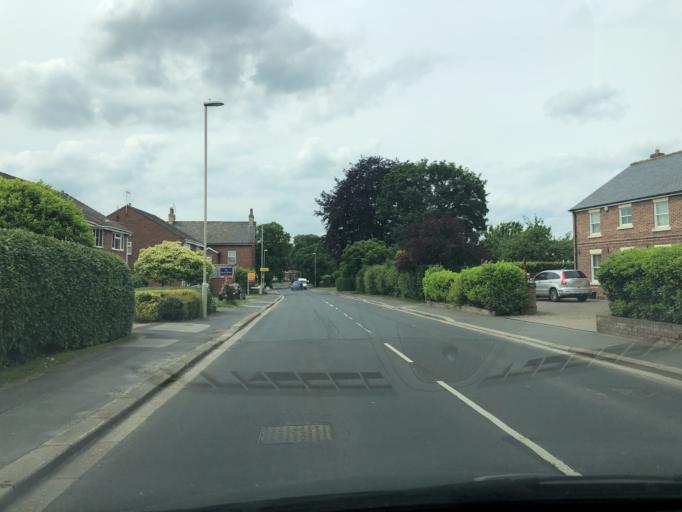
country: GB
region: England
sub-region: North Yorkshire
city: Pickering
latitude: 54.2402
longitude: -0.7640
